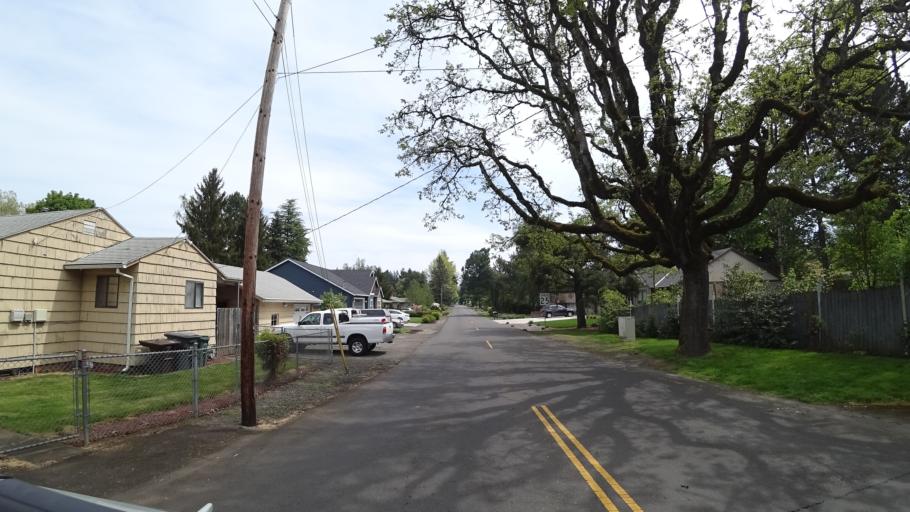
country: US
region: Oregon
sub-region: Washington County
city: Hillsboro
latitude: 45.5122
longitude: -122.9496
